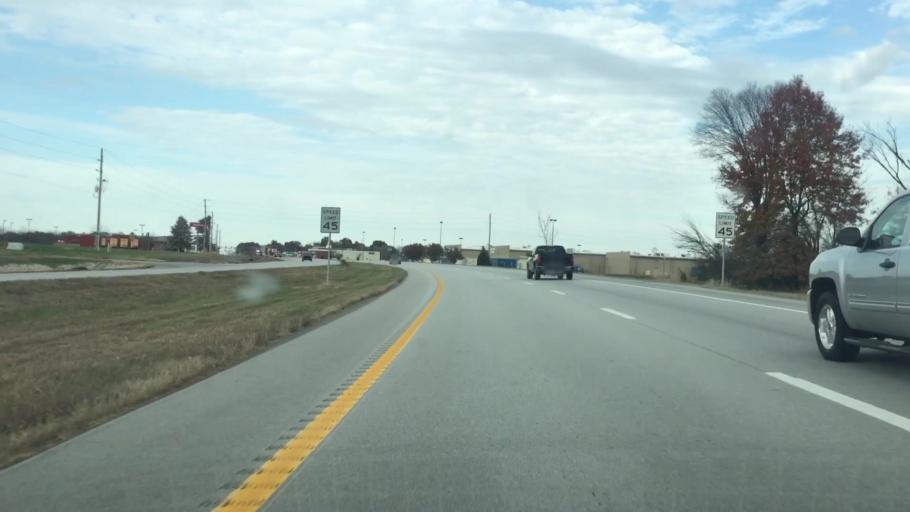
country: US
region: Missouri
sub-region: Henry County
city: Clinton
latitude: 38.3603
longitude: -93.7526
